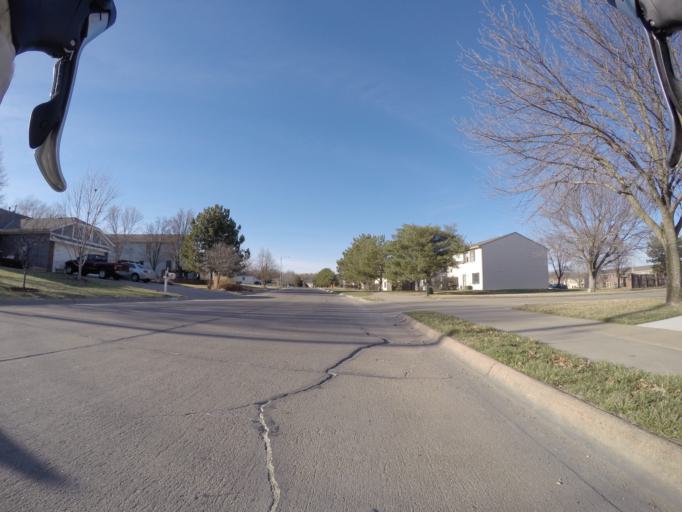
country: US
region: Kansas
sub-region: Riley County
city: Manhattan
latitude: 39.2114
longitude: -96.6188
